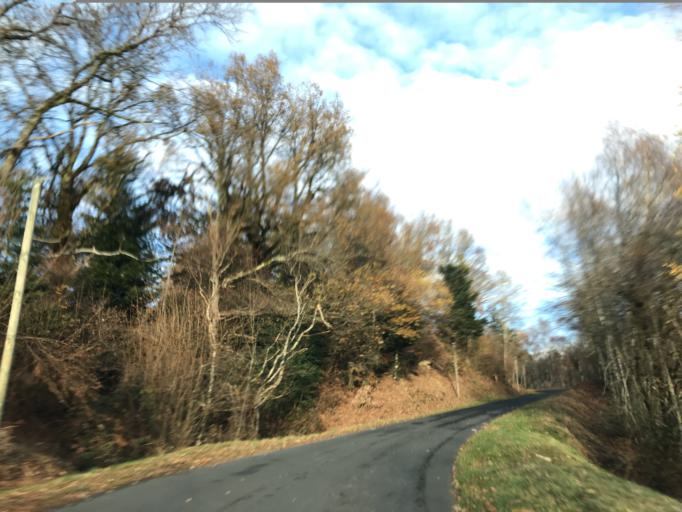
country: FR
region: Auvergne
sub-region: Departement du Puy-de-Dome
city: Celles-sur-Durolle
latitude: 45.7746
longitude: 3.6663
